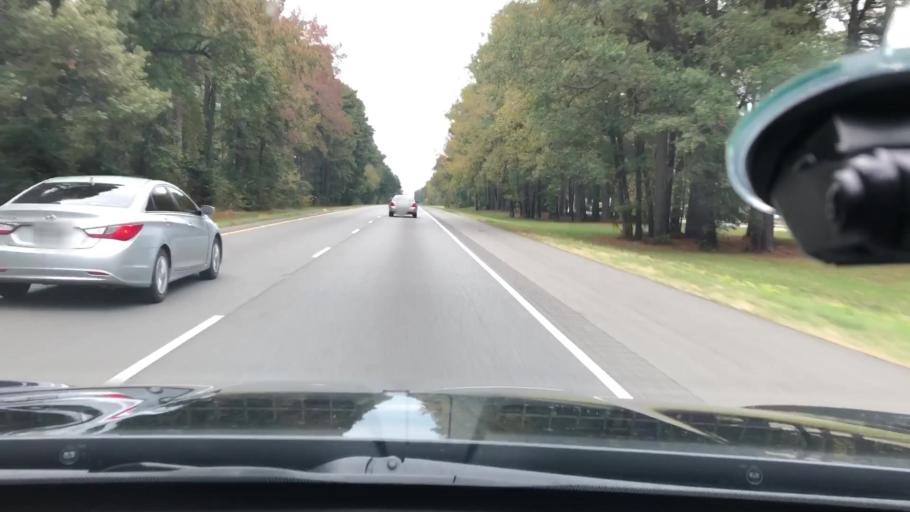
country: US
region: Arkansas
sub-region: Hempstead County
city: Hope
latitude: 33.6495
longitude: -93.6728
